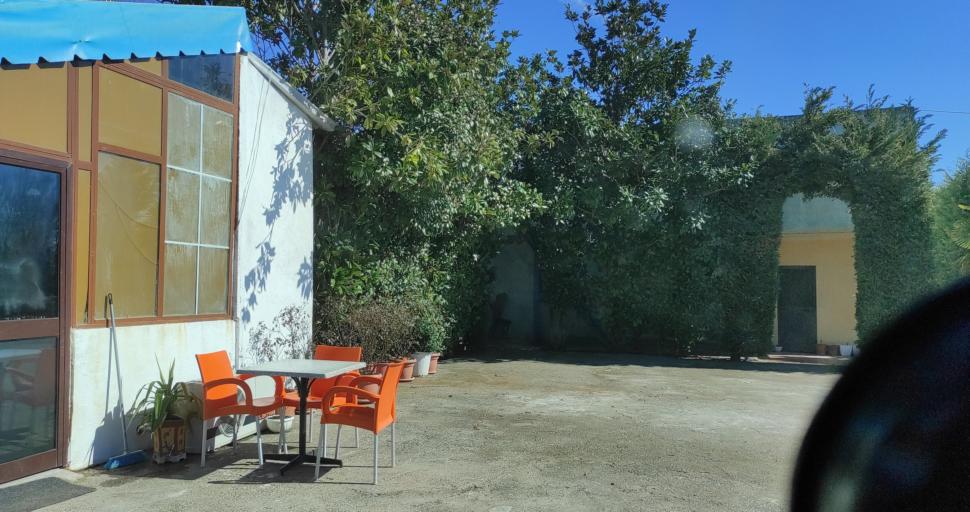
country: AL
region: Shkoder
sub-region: Rrethi i Shkodres
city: Velipoje
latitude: 41.8668
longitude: 19.4061
